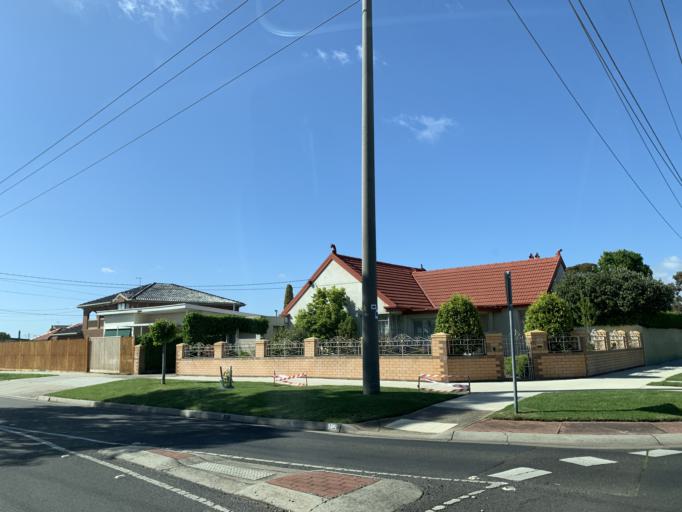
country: AU
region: Victoria
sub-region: Brimbank
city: Saint Albans
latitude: -37.7367
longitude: 144.8098
